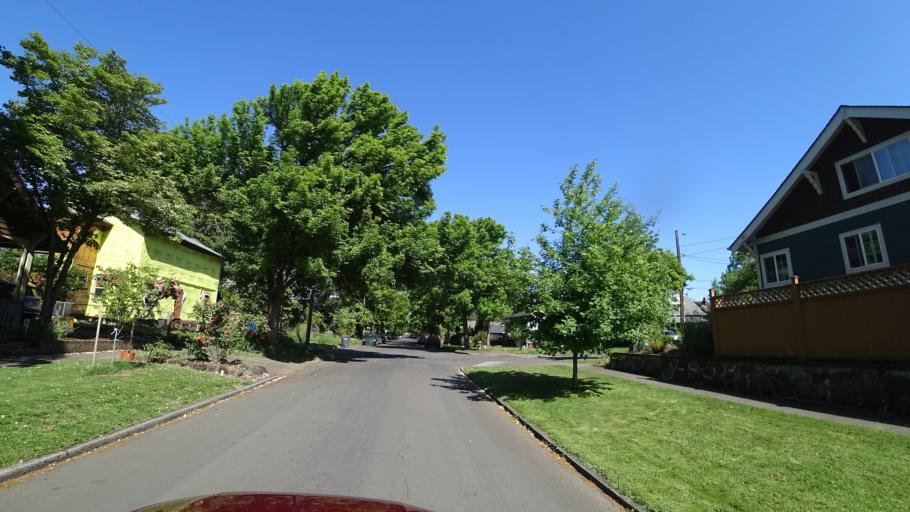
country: US
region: Oregon
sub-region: Multnomah County
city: Lents
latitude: 45.4920
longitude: -122.6162
